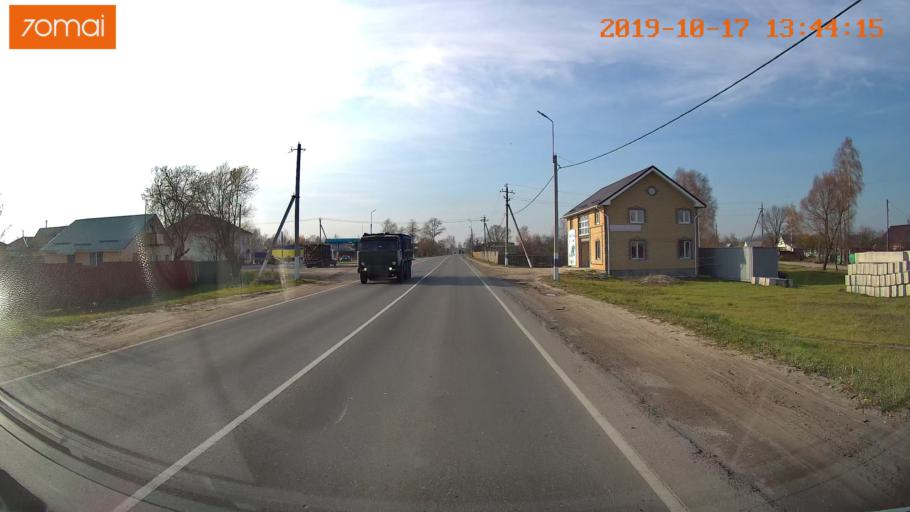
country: RU
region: Rjazan
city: Tuma
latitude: 55.1461
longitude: 40.5320
